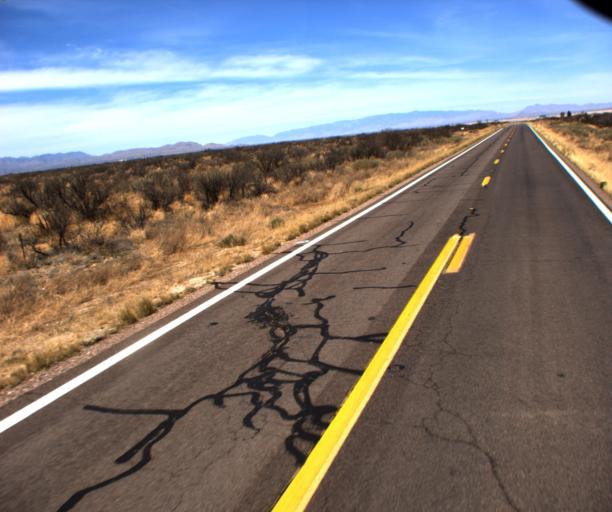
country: US
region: Arizona
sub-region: Cochise County
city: Willcox
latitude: 32.1113
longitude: -109.9132
